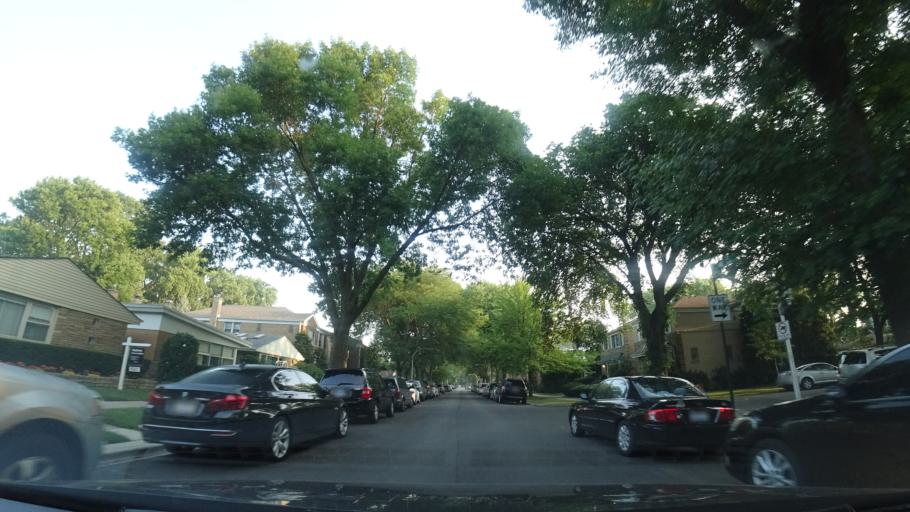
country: US
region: Illinois
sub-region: Cook County
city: Lincolnwood
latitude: 41.9782
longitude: -87.7036
